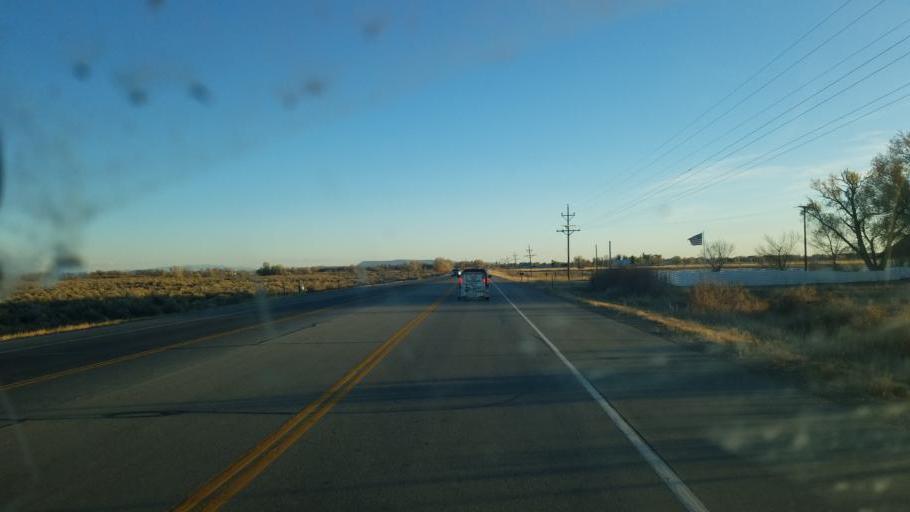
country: US
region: Colorado
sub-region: Alamosa County
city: Alamosa East
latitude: 37.5019
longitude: -105.8581
